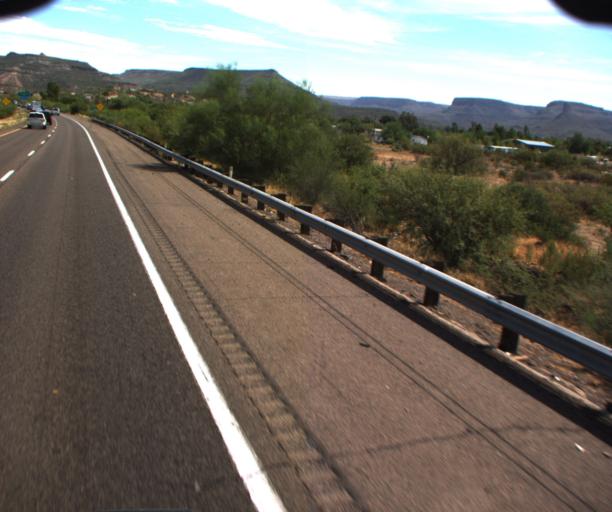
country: US
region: Arizona
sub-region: Yavapai County
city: Black Canyon City
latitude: 34.0722
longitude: -112.1402
